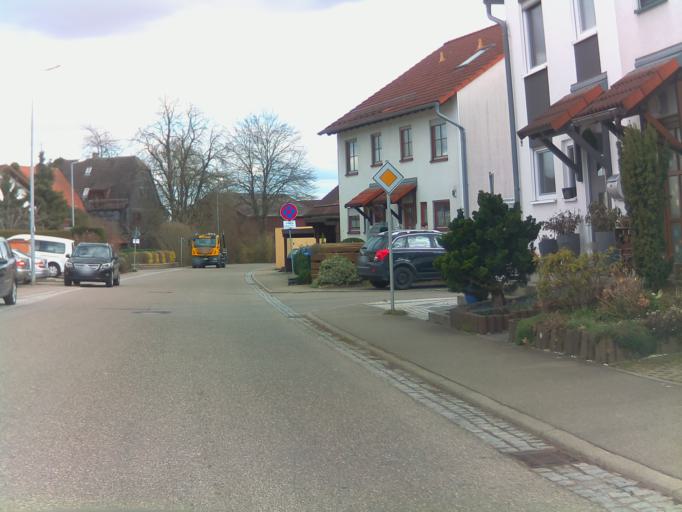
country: DE
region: Baden-Wuerttemberg
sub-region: Regierungsbezirk Stuttgart
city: Alfdorf
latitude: 48.8439
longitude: 9.7084
